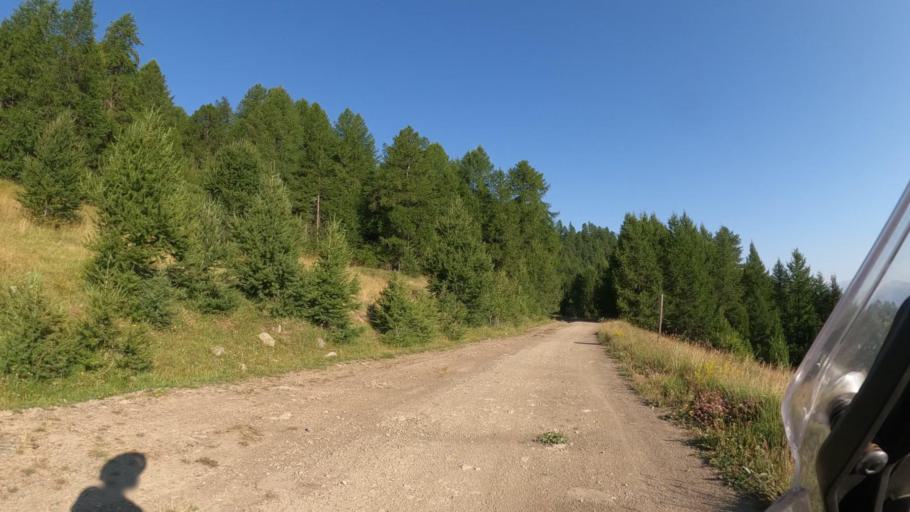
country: FR
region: Provence-Alpes-Cote d'Azur
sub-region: Departement des Hautes-Alpes
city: Guillestre
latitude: 44.6124
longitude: 6.6473
